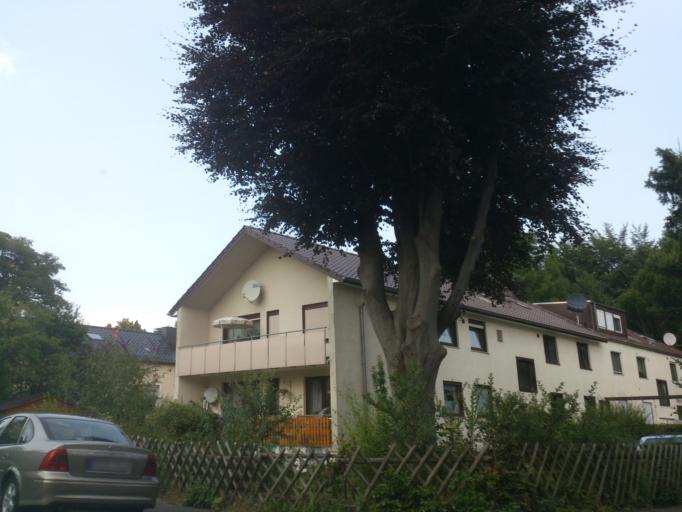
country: DE
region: North Rhine-Westphalia
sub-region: Regierungsbezirk Detmold
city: Paderborn
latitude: 51.7162
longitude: 8.7240
